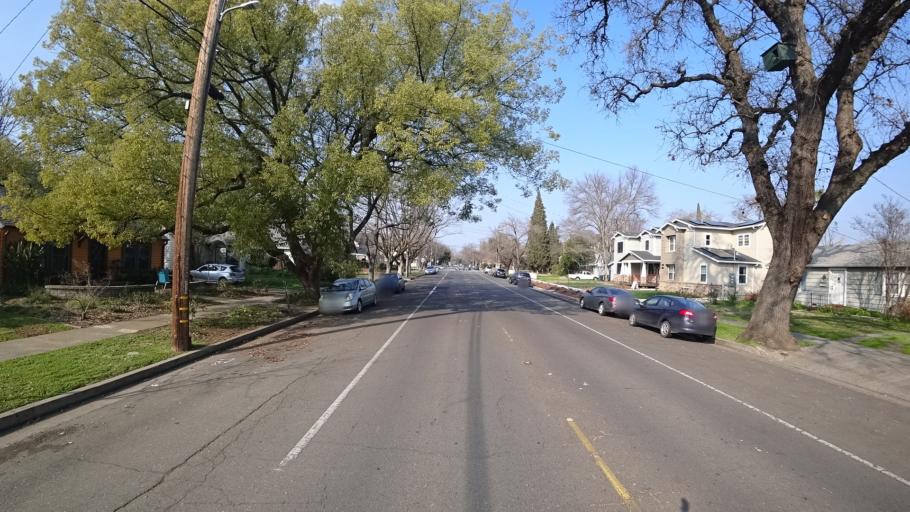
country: US
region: California
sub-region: Yolo County
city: Davis
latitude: 38.5471
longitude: -121.7364
